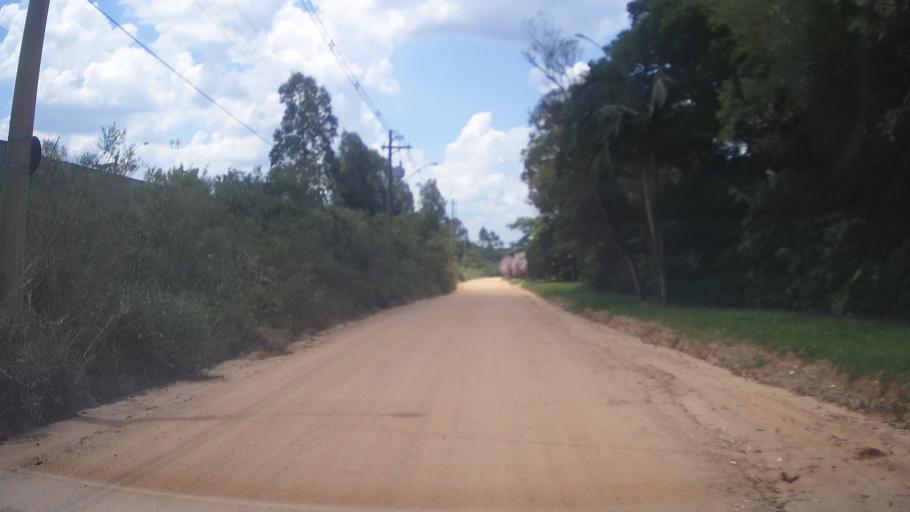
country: BR
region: Sao Paulo
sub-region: Jundiai
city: Jundiai
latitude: -23.1604
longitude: -46.8913
